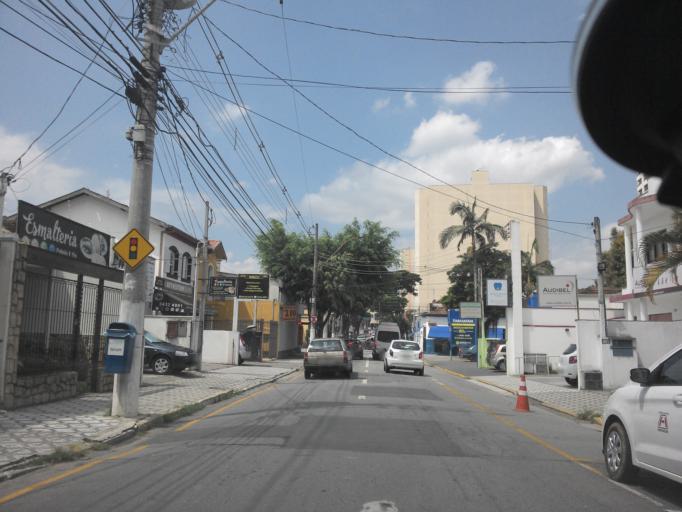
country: BR
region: Sao Paulo
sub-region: Taubate
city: Taubate
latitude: -23.0226
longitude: -45.5550
